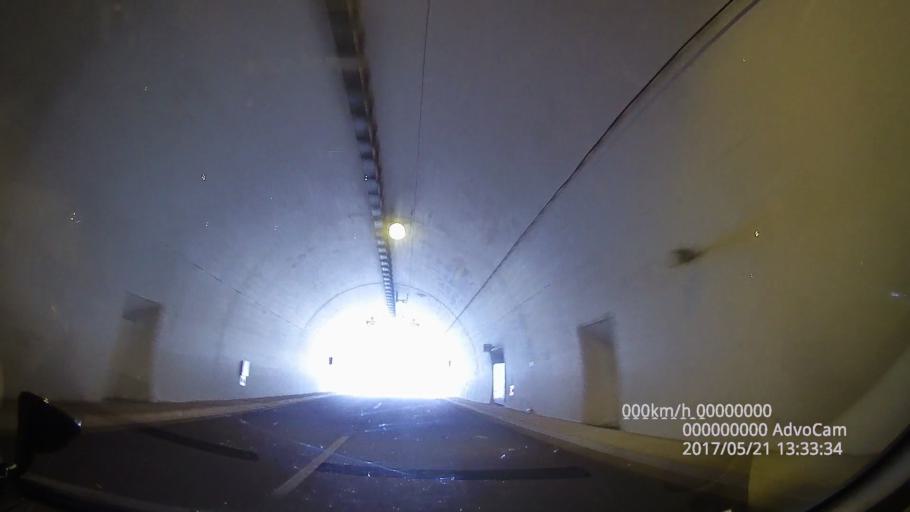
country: GR
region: Central Greece
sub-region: Nomos Fthiotidos
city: Stylida
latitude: 38.9211
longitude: 22.6092
